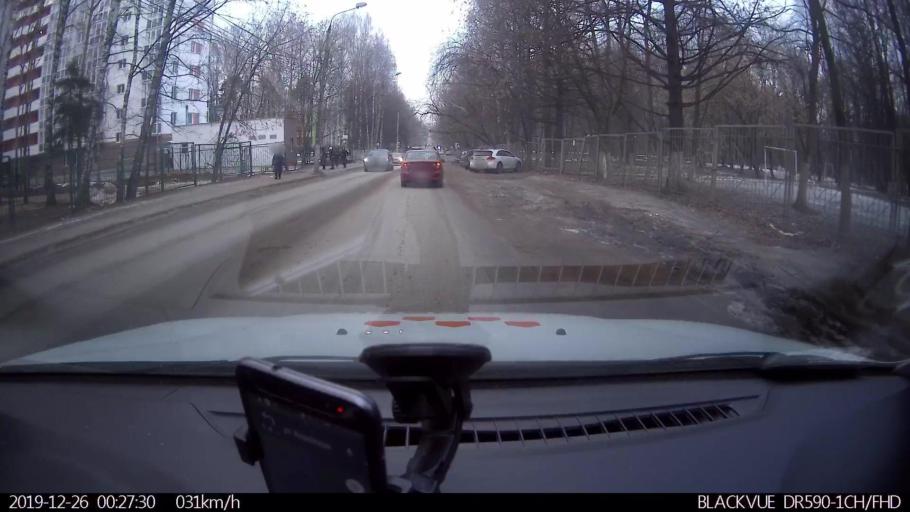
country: RU
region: Nizjnij Novgorod
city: Nizhniy Novgorod
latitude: 56.2643
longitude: 43.9987
